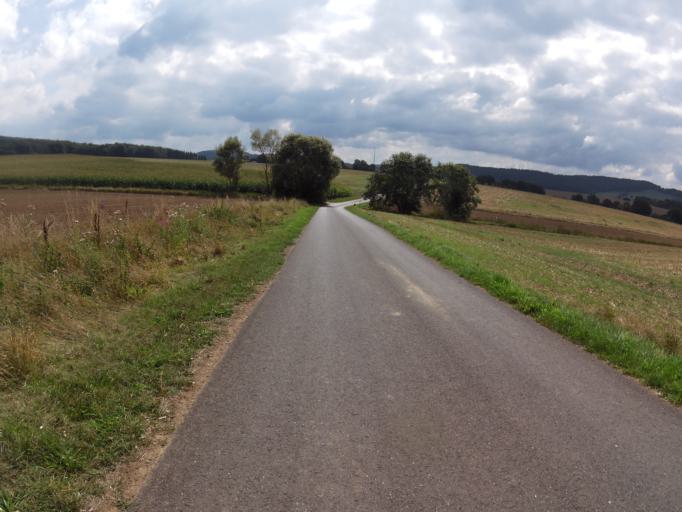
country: DE
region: Rheinland-Pfalz
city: Oberbettingen
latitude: 50.2812
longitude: 6.6473
